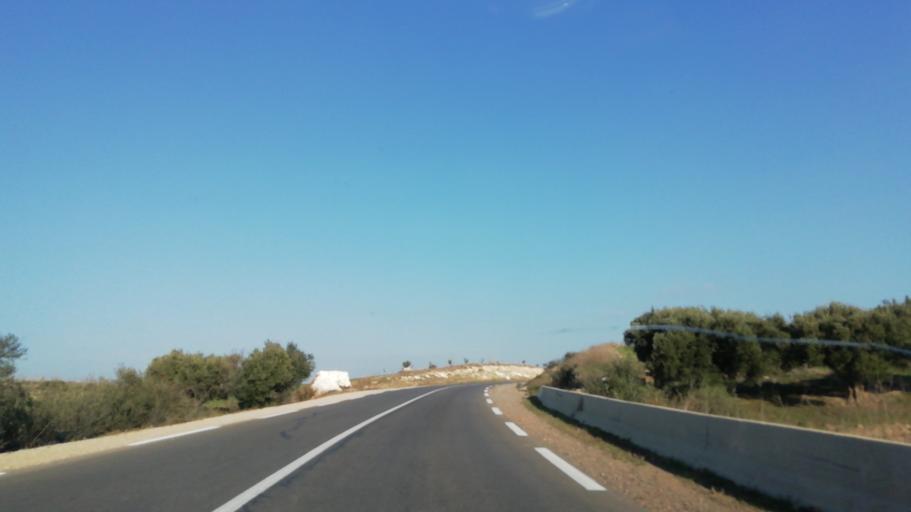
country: DZ
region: Sidi Bel Abbes
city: Sidi Bel Abbes
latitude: 35.1653
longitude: -0.8615
